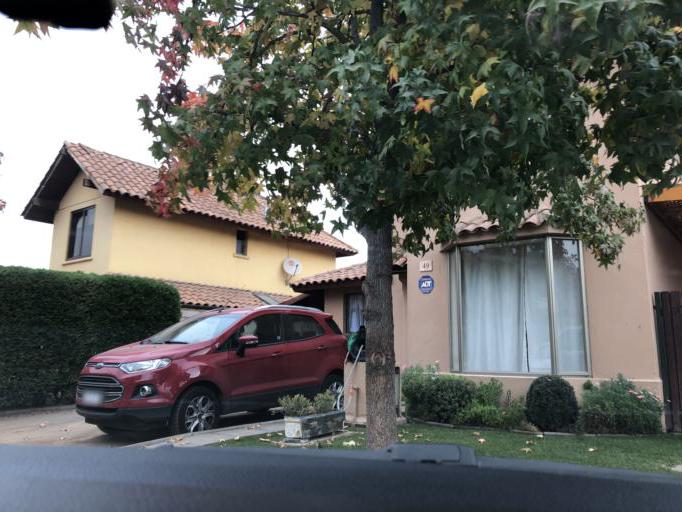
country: CL
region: Santiago Metropolitan
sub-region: Provincia de Cordillera
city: Puente Alto
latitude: -33.5886
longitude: -70.5108
